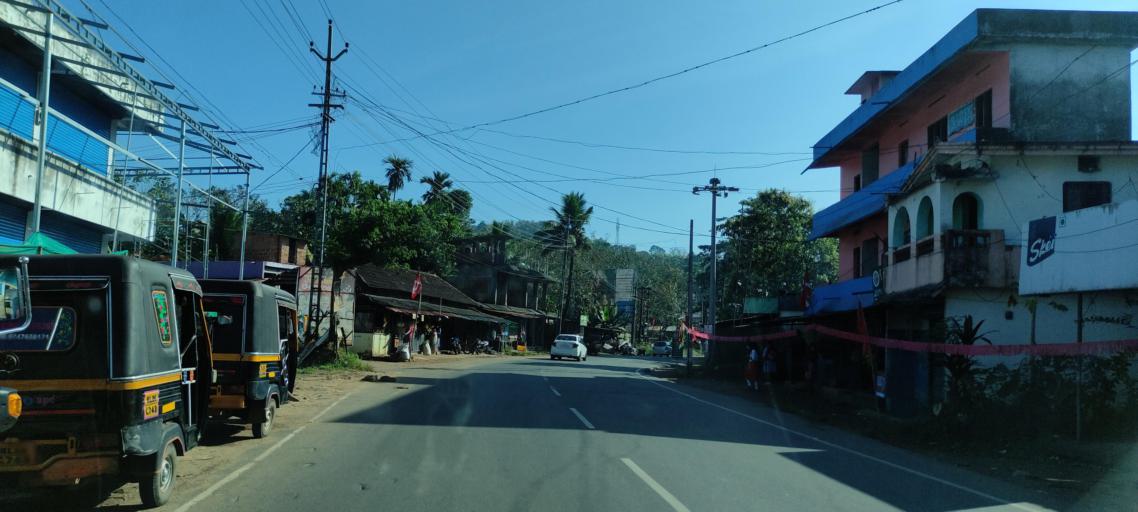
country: IN
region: Kerala
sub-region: Pattanamtitta
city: Adur
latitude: 9.1671
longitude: 76.6770
